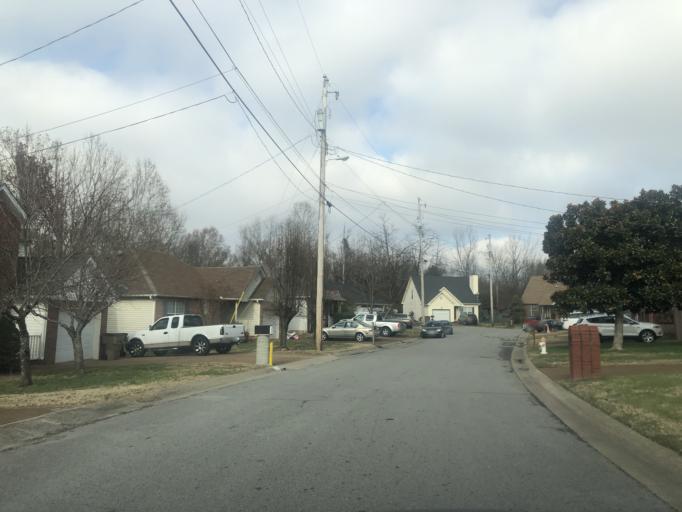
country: US
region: Tennessee
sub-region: Rutherford County
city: La Vergne
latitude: 36.0852
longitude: -86.6515
